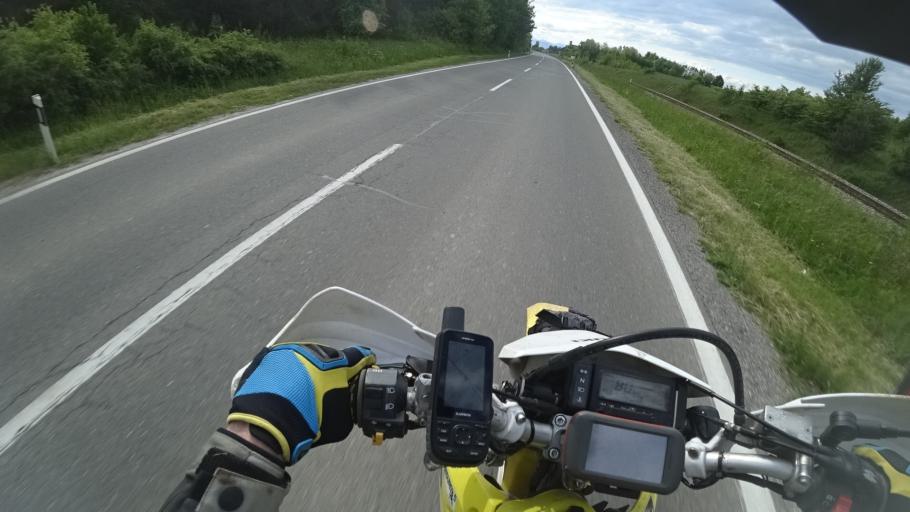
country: HR
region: Licko-Senjska
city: Gospic
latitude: 44.5261
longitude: 15.4101
